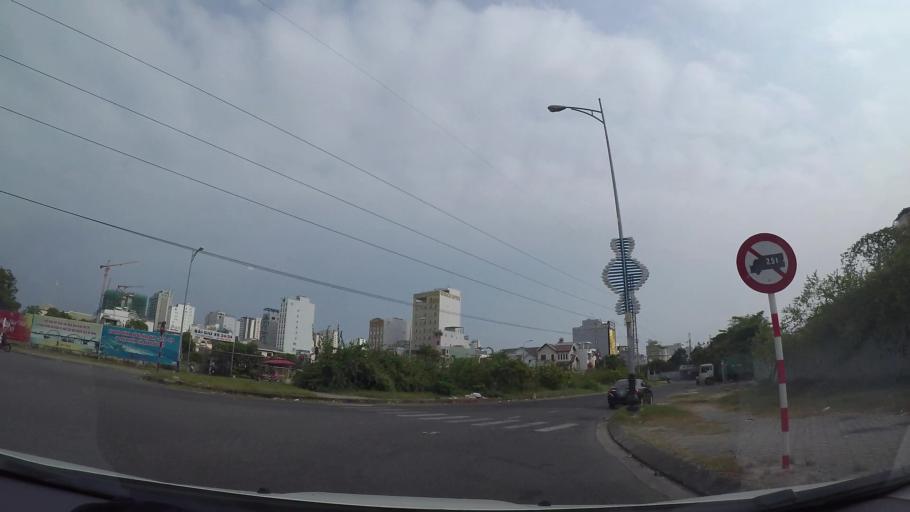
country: VN
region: Da Nang
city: Son Tra
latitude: 16.0697
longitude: 108.2396
